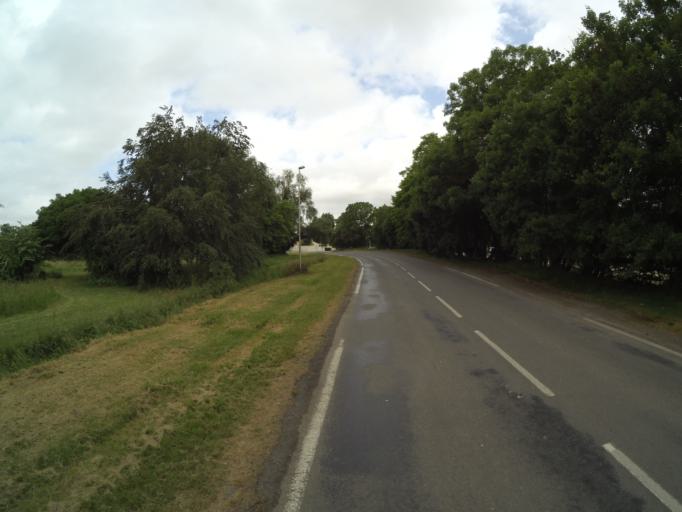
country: FR
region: Poitou-Charentes
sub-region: Departement de la Charente-Maritime
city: Saint-Laurent-de-la-Pree
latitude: 45.9927
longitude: -1.0279
